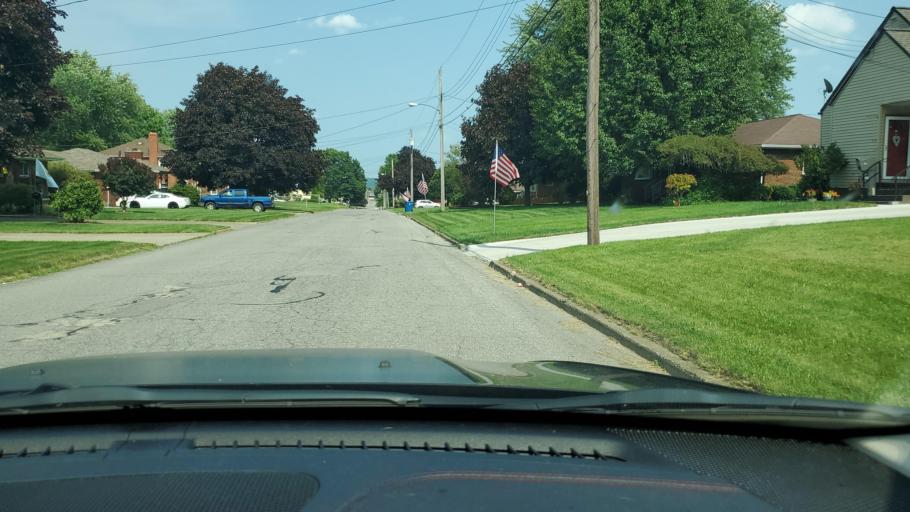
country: US
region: Ohio
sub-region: Mahoning County
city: Struthers
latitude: 41.0491
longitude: -80.6143
